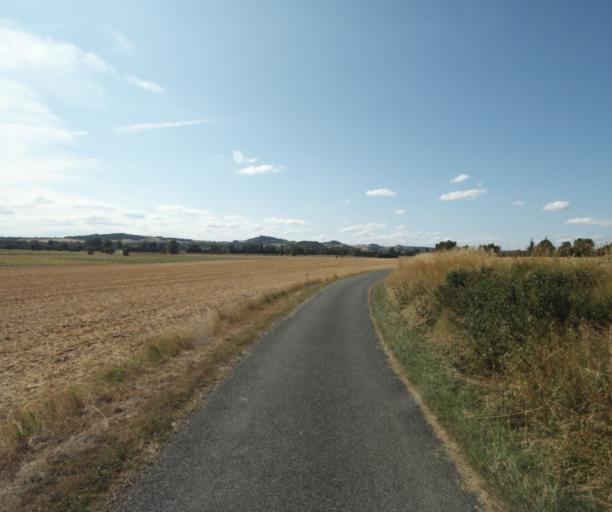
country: FR
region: Midi-Pyrenees
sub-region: Departement de la Haute-Garonne
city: Revel
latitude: 43.5019
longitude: 1.9761
